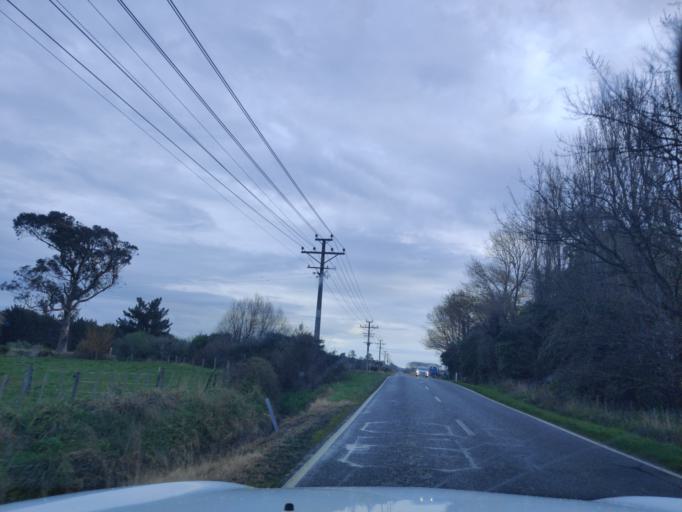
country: NZ
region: Manawatu-Wanganui
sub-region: Palmerston North City
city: Palmerston North
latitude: -40.3480
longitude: 175.7034
